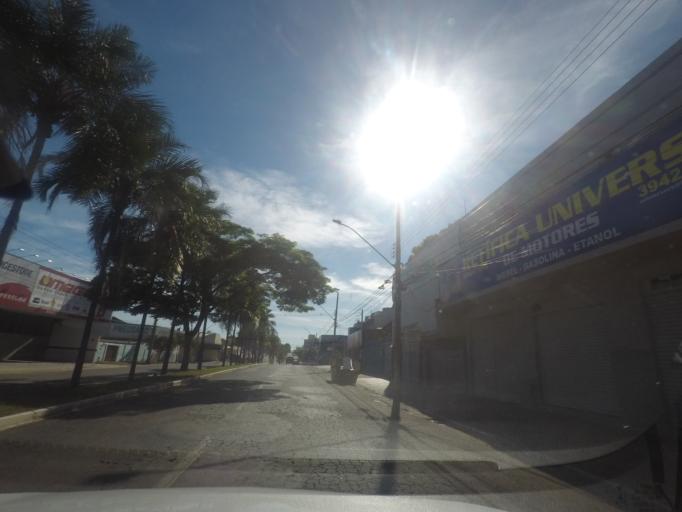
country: BR
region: Goias
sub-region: Goiania
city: Goiania
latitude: -16.6667
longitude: -49.2695
